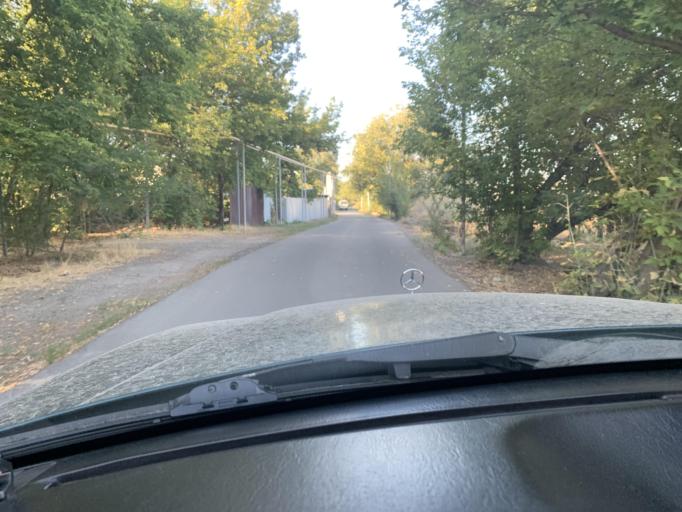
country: KZ
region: Almaty Oblysy
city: Energeticheskiy
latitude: 43.3933
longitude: 77.0006
